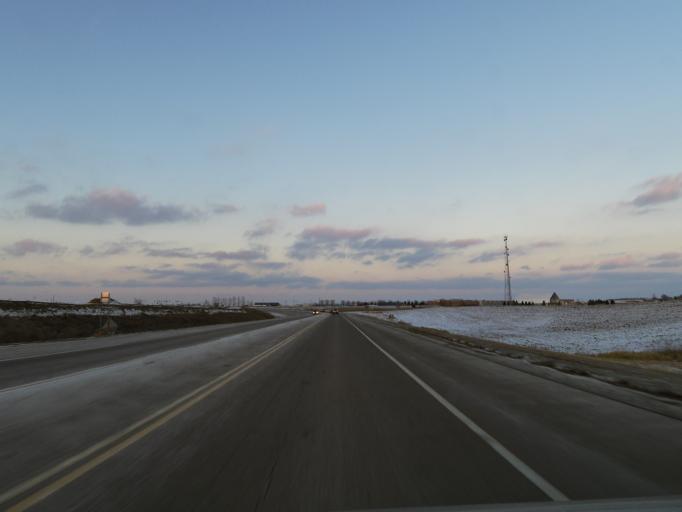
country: US
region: Minnesota
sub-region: Dakota County
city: Rosemount
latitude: 44.7121
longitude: -93.1325
